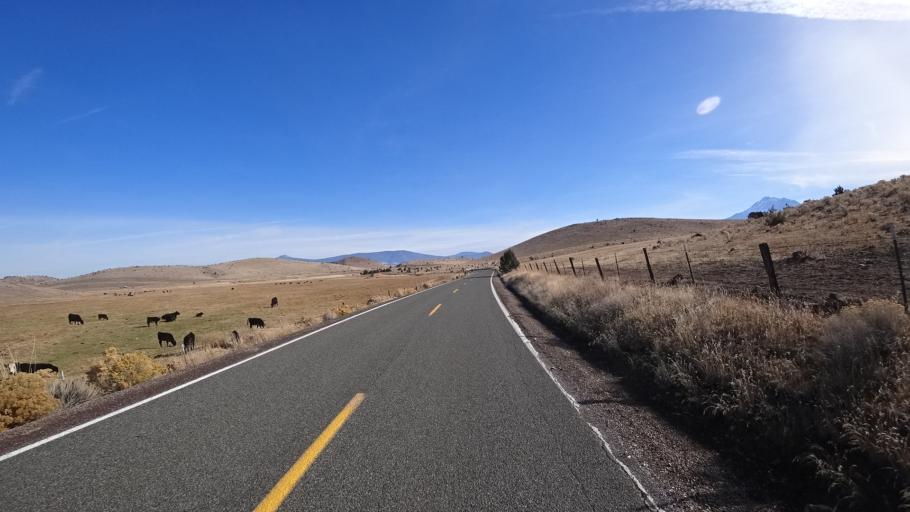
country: US
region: California
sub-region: Siskiyou County
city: Weed
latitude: 41.5495
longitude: -122.4950
